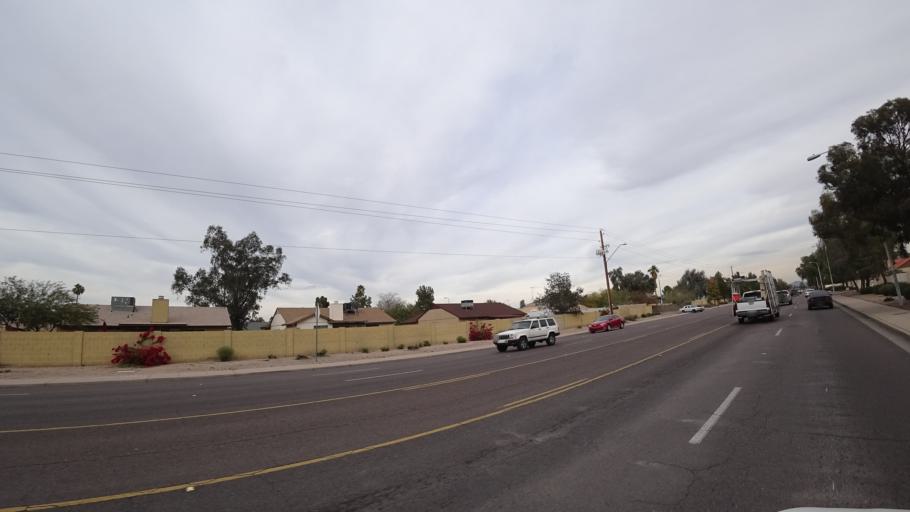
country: US
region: Arizona
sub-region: Maricopa County
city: Peoria
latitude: 33.5817
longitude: -112.2002
